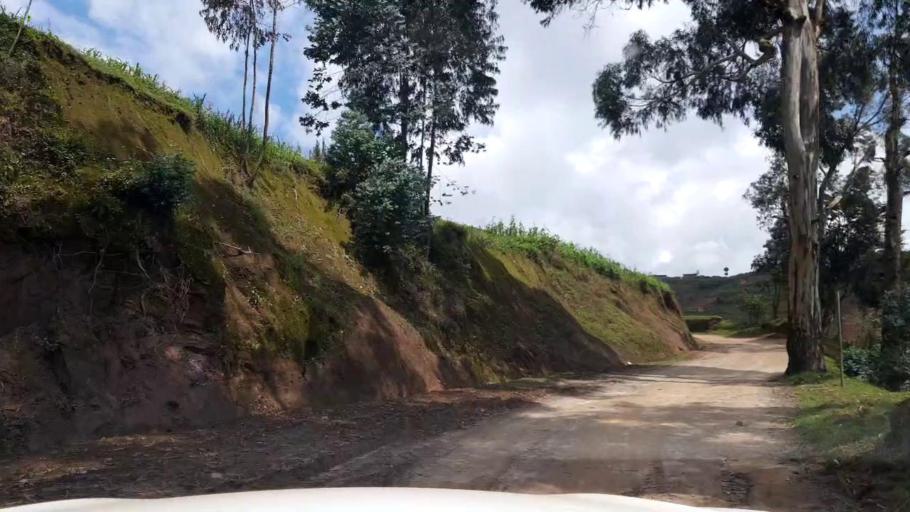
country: RW
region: Western Province
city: Kibuye
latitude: -1.9224
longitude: 29.4548
